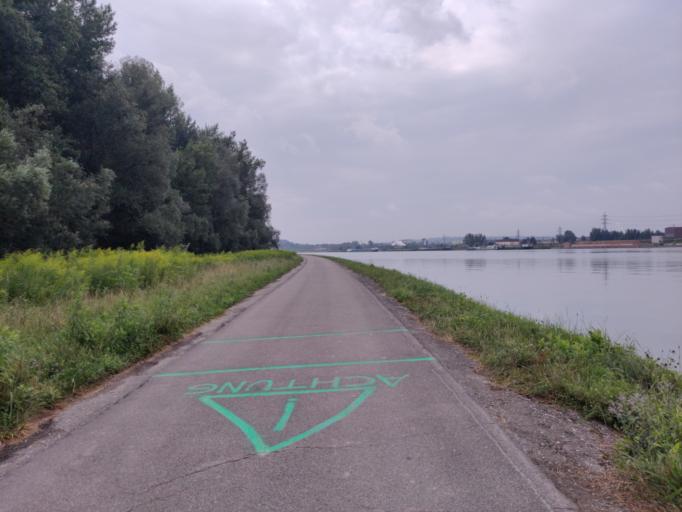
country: AT
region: Upper Austria
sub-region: Politischer Bezirk Urfahr-Umgebung
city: Steyregg
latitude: 48.2857
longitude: 14.3460
